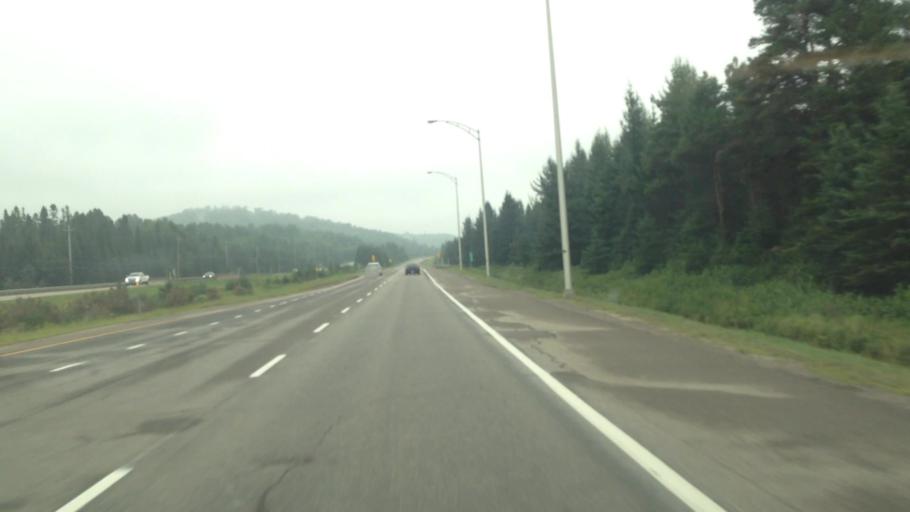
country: CA
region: Quebec
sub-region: Laurentides
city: Sainte-Agathe-des-Monts
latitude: 46.0971
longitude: -74.3554
